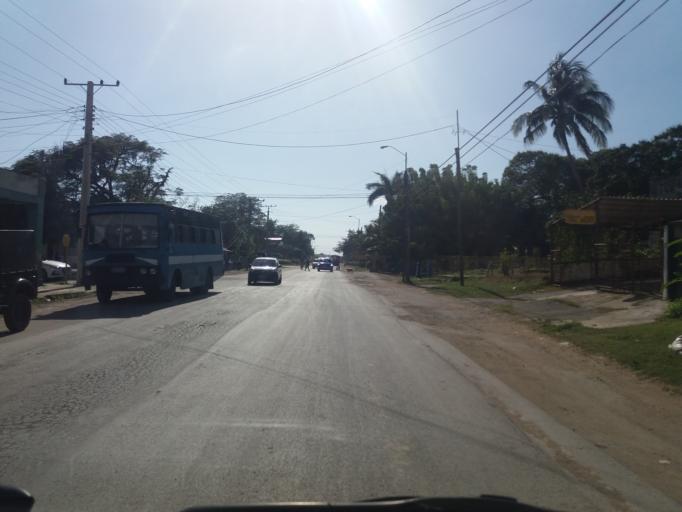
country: CU
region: Cienfuegos
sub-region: Municipio de Cienfuegos
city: Cienfuegos
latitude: 22.1564
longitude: -80.4309
